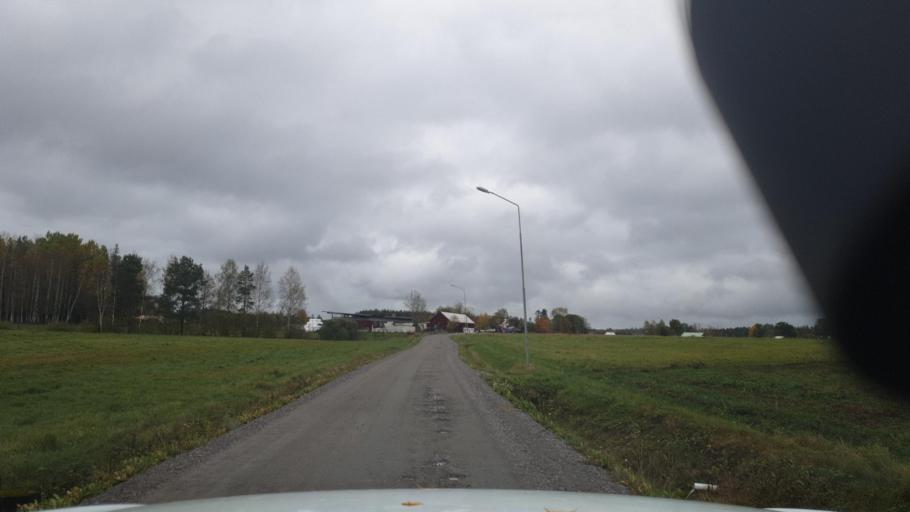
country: SE
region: Vaermland
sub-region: Karlstads Kommun
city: Edsvalla
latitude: 59.4916
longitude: 13.1699
